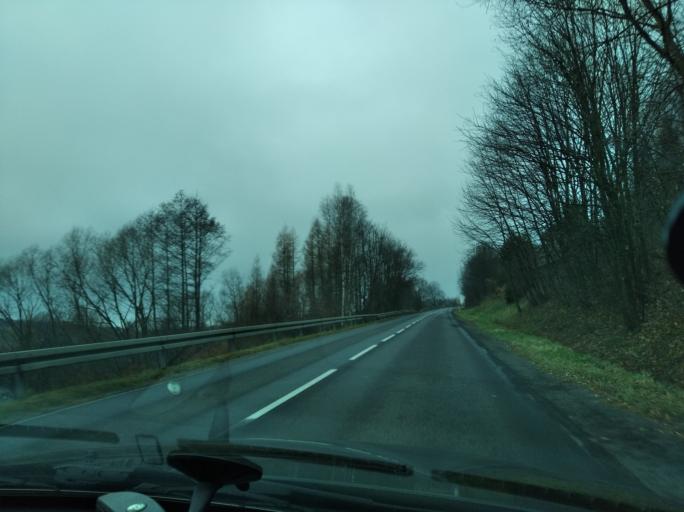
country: PL
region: Subcarpathian Voivodeship
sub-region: Powiat przeworski
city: Jawornik Polski
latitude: 49.8830
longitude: 22.2397
